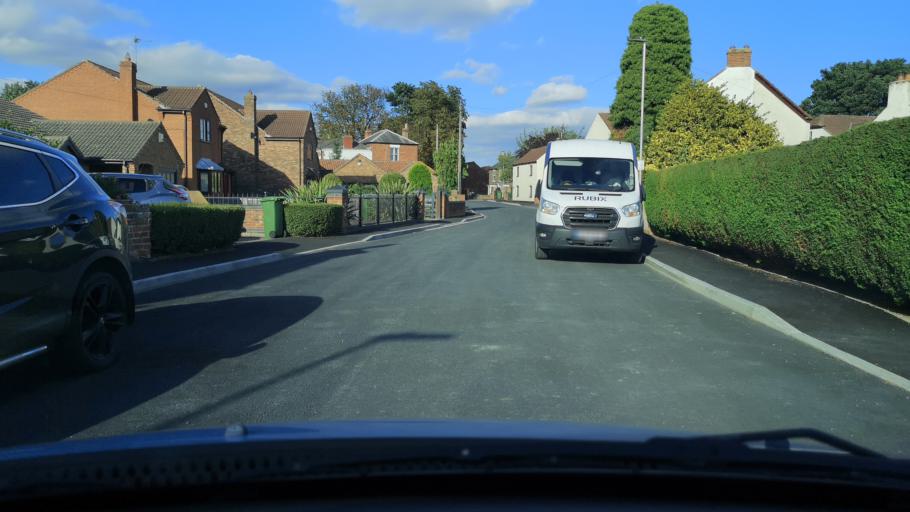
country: GB
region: England
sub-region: North Lincolnshire
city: Gunness
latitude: 53.5777
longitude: -0.7405
